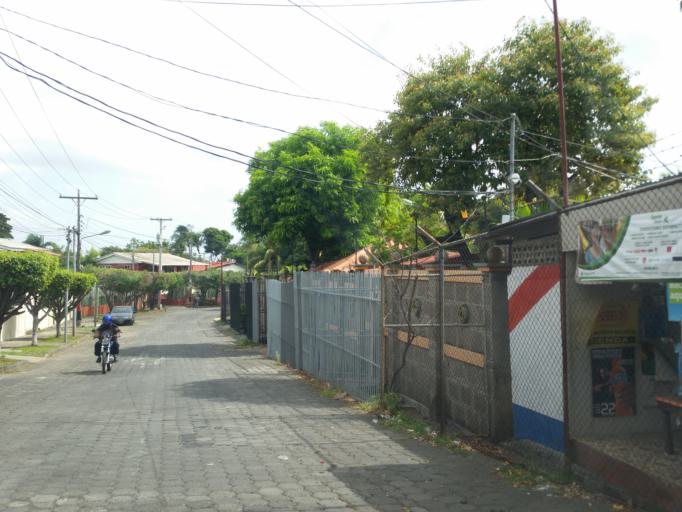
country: NI
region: Managua
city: Managua
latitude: 12.1149
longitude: -86.2766
